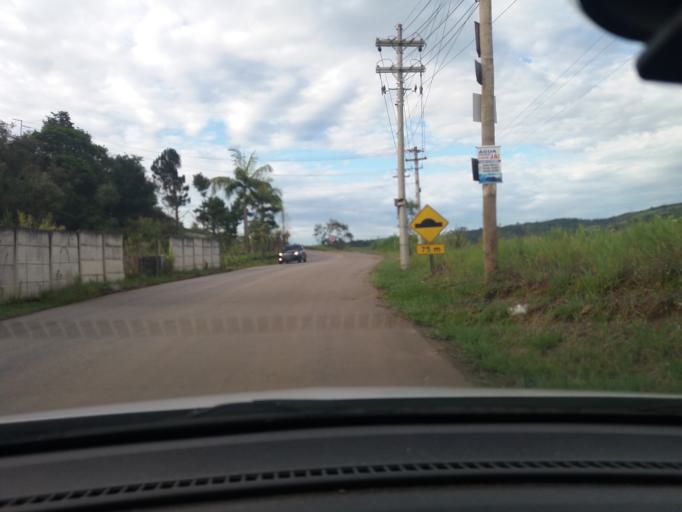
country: BR
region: Sao Paulo
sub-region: Bom Jesus Dos Perdoes
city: Bom Jesus dos Perdoes
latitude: -23.1620
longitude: -46.4491
